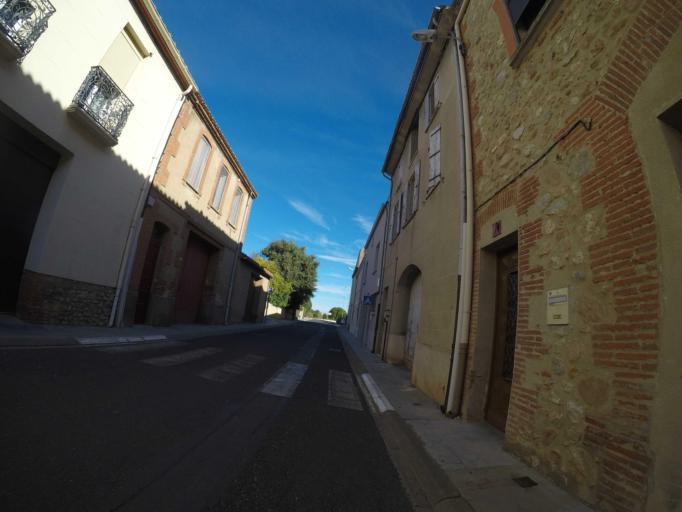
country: FR
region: Languedoc-Roussillon
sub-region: Departement des Pyrenees-Orientales
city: Villemolaque
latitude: 42.5791
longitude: 2.8125
